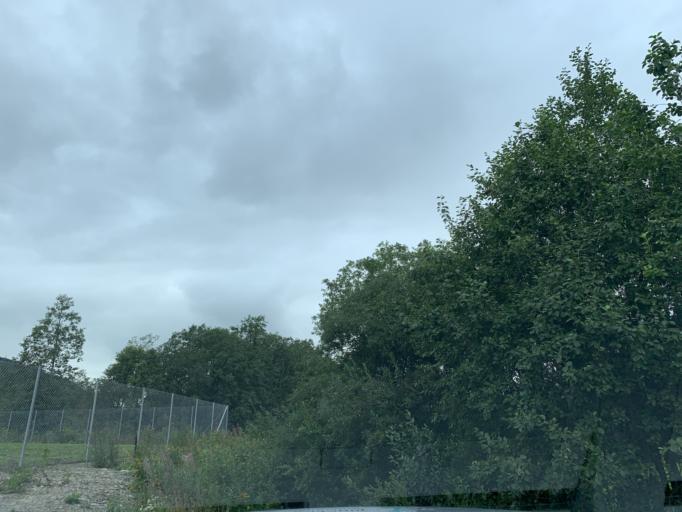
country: NO
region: Oppland
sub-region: Ringebu
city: Ringebu
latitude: 61.5262
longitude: 10.1226
